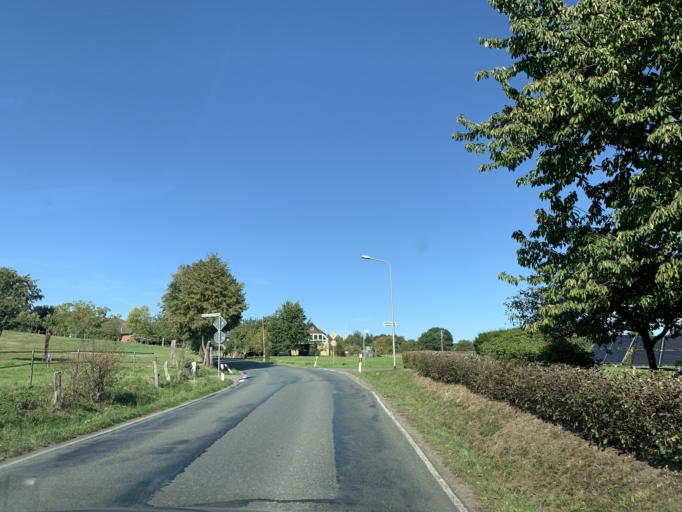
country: DE
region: North Rhine-Westphalia
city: Porta Westfalica
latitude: 52.1984
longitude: 8.9720
